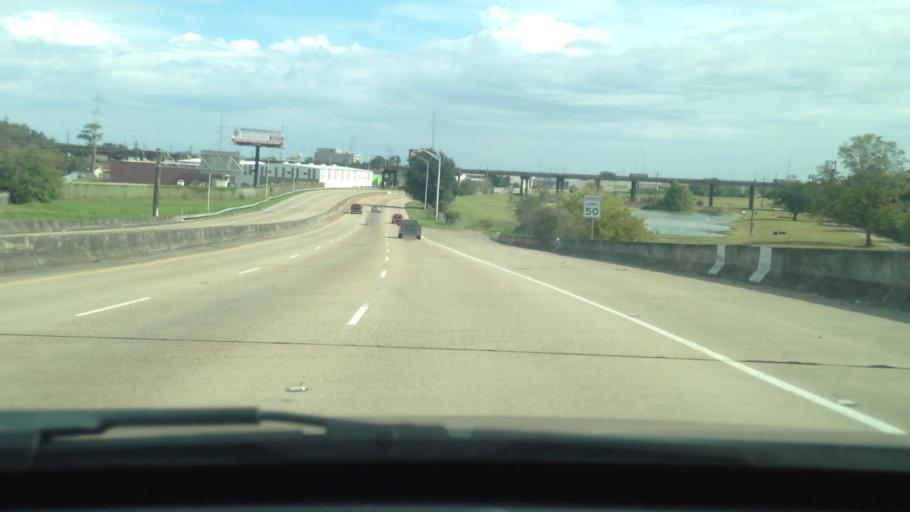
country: US
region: Louisiana
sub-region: Jefferson Parish
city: Metairie Terrace
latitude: 29.9709
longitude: -90.1607
